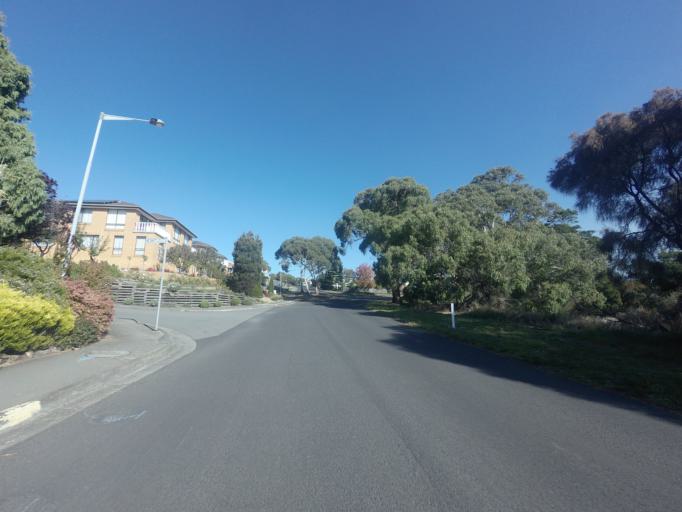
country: AU
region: Tasmania
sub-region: Clarence
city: Bellerive
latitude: -42.8697
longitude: 147.3541
